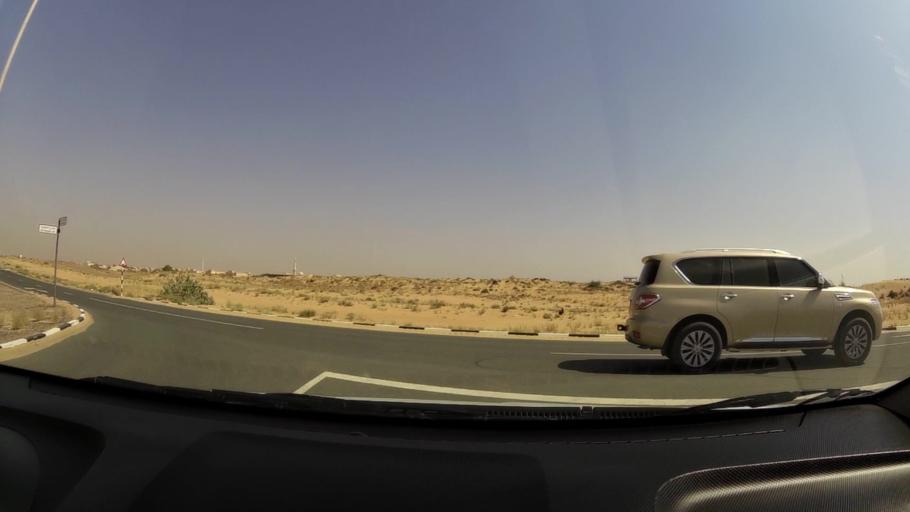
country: AE
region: Umm al Qaywayn
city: Umm al Qaywayn
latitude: 25.4810
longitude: 55.6081
